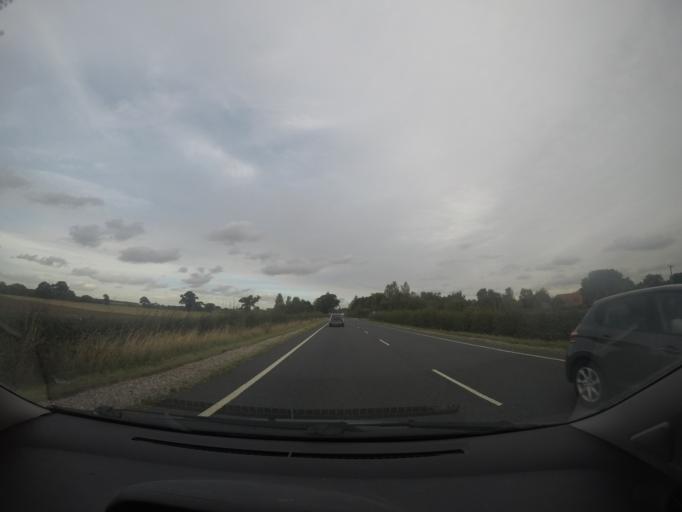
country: GB
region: England
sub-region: North Yorkshire
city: Riccall
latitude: 53.8465
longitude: -1.0532
